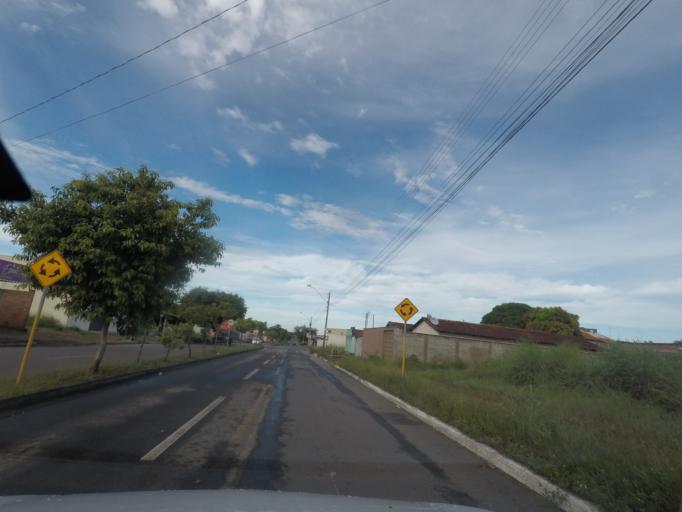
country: BR
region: Goias
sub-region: Aparecida De Goiania
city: Aparecida de Goiania
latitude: -16.7872
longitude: -49.3657
